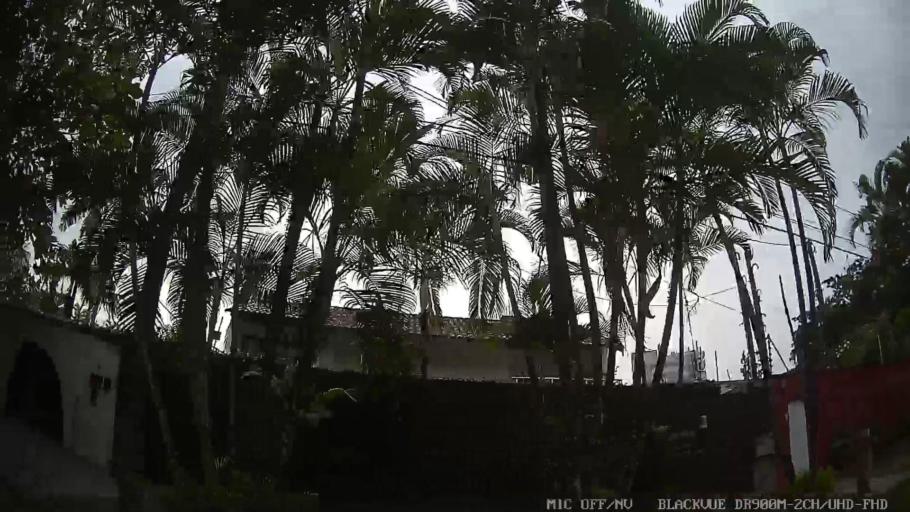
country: BR
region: Sao Paulo
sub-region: Guaruja
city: Guaruja
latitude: -23.9830
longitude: -46.2101
